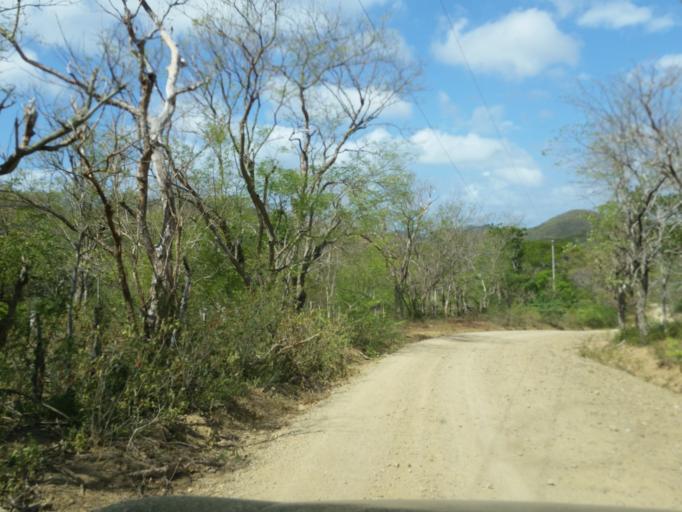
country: CR
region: Guanacaste
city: La Cruz
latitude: 11.1048
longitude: -85.7377
